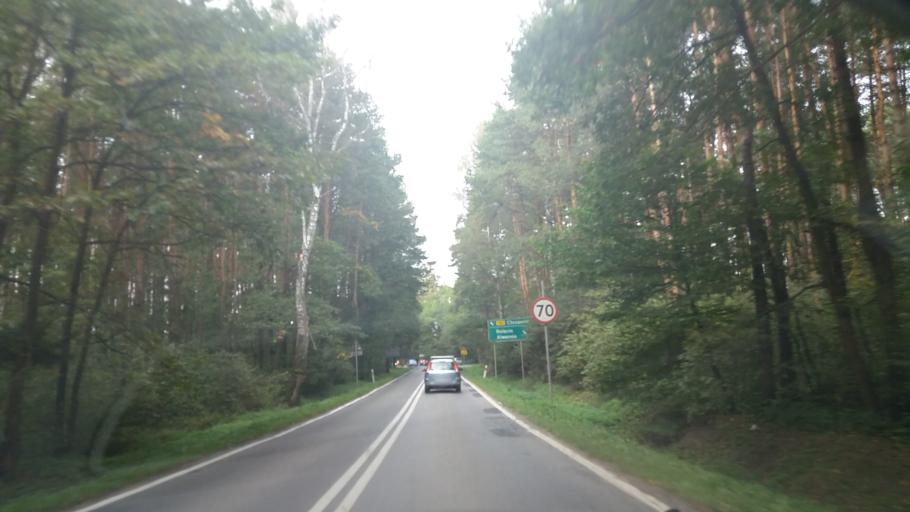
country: PL
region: Lesser Poland Voivodeship
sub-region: Powiat chrzanowski
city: Pogorzyce
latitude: 50.1220
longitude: 19.4354
